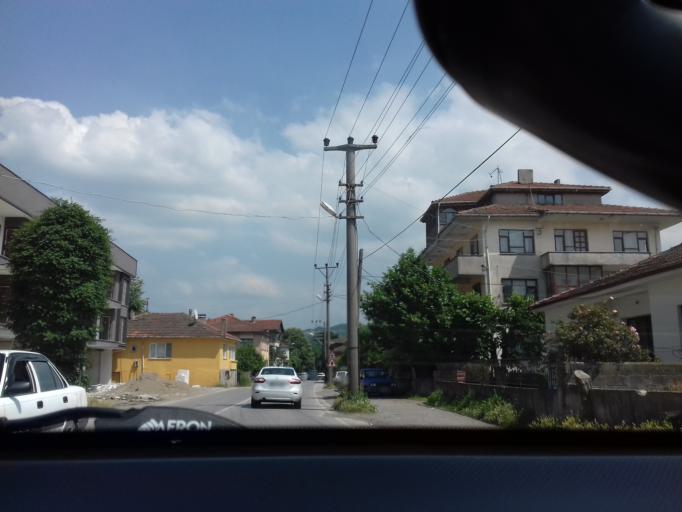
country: TR
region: Sakarya
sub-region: Merkez
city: Sapanca
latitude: 40.6892
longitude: 30.2631
